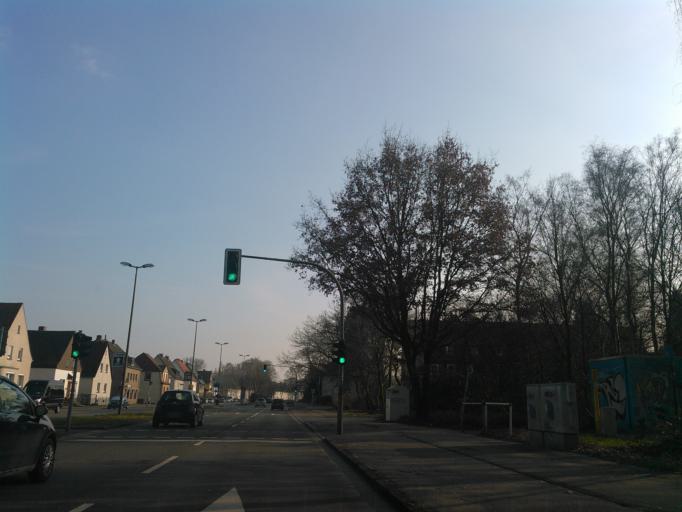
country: DE
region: North Rhine-Westphalia
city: Marl
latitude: 51.6675
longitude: 7.1042
